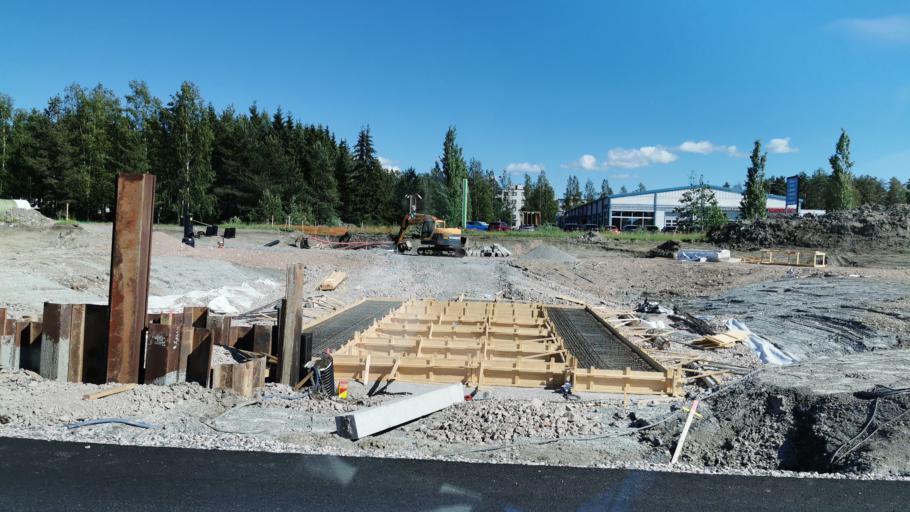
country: FI
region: Varsinais-Suomi
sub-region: Loimaa
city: Loimaa
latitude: 60.8516
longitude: 23.0346
